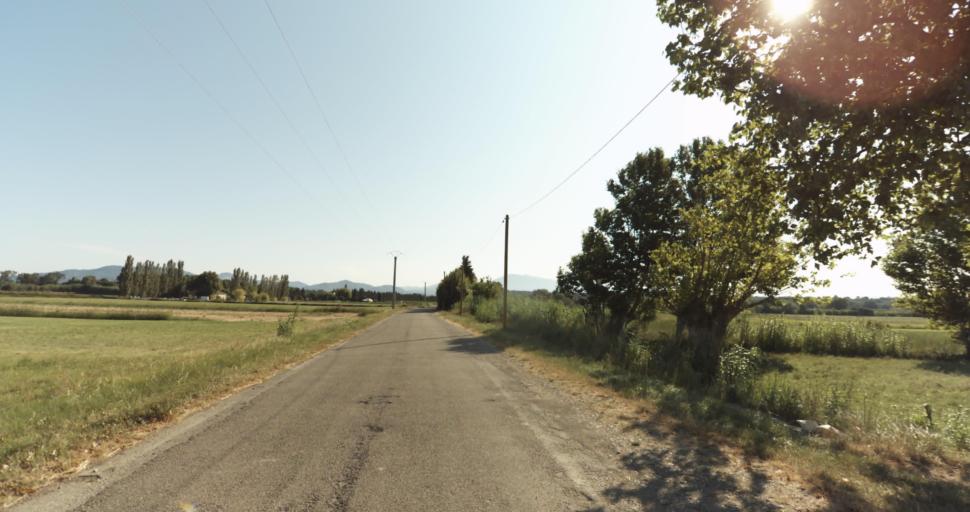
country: FR
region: Provence-Alpes-Cote d'Azur
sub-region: Departement du Vaucluse
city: Sarrians
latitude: 44.0588
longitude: 4.9732
